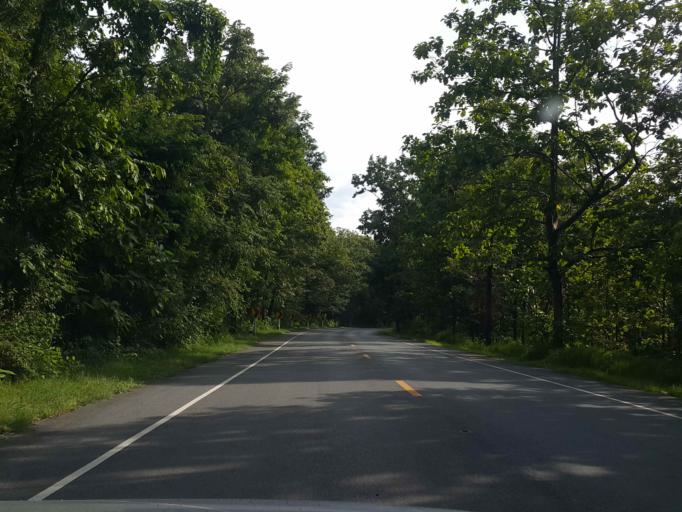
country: TH
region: Uttaradit
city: Lap Lae
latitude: 17.8211
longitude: 99.8644
